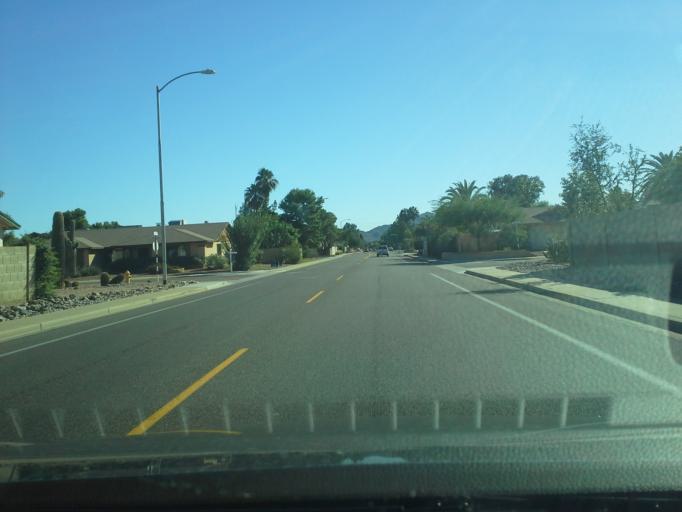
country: US
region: Arizona
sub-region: Maricopa County
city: Paradise Valley
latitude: 33.6142
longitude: -111.9866
